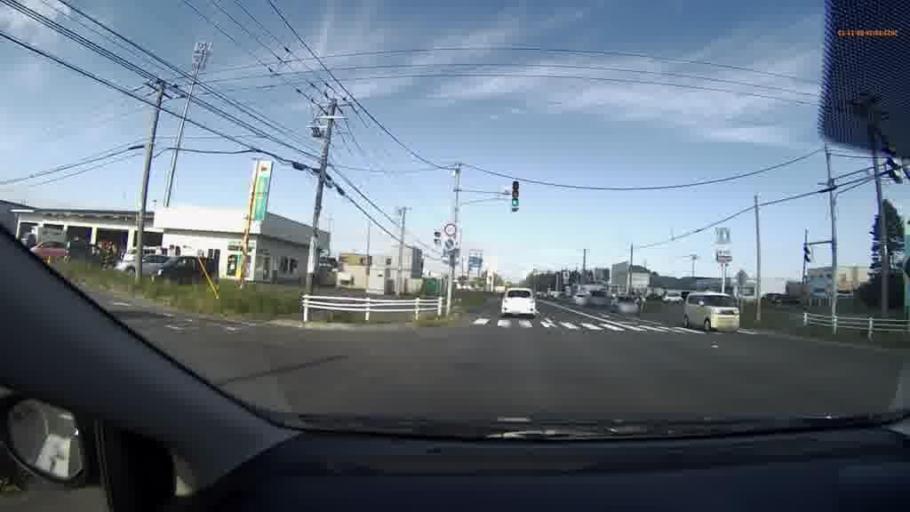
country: JP
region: Hokkaido
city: Kushiro
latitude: 43.0124
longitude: 144.4080
